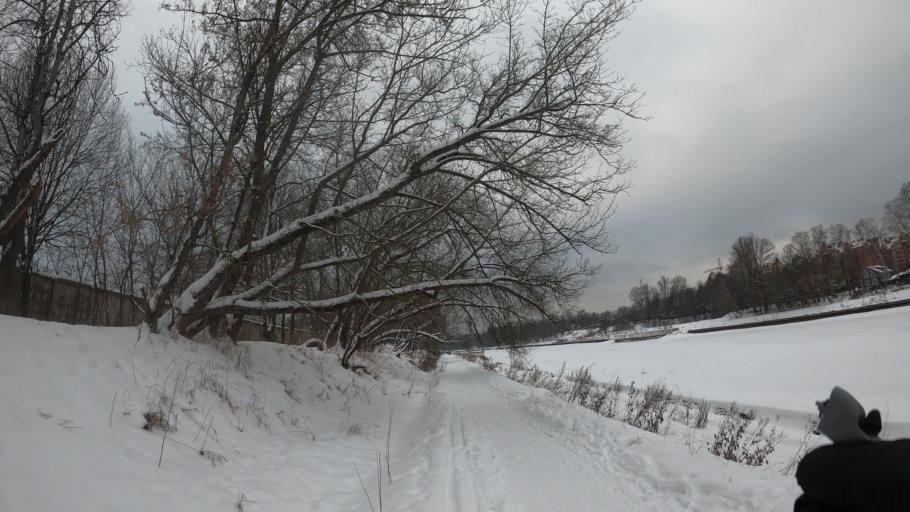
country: RU
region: Moskovskaya
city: Dolgoprudnyy
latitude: 55.9522
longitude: 37.4823
